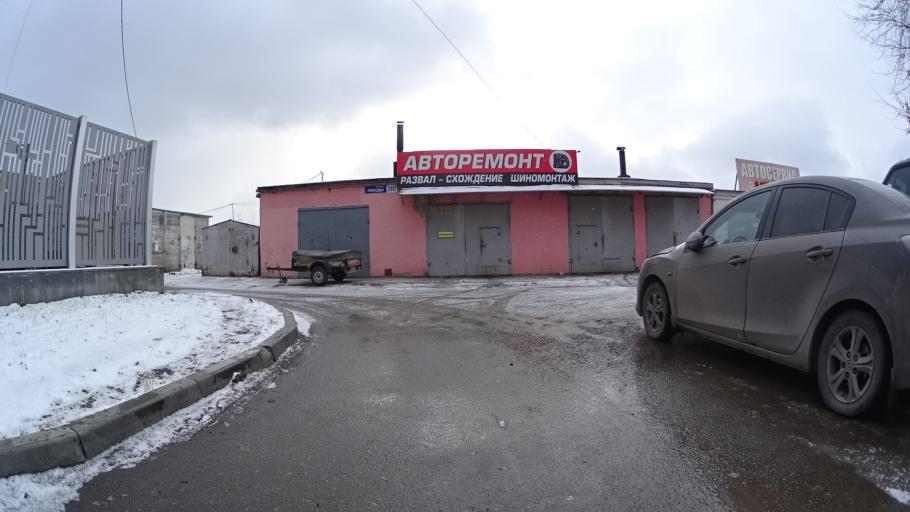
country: RU
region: Chelyabinsk
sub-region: Gorod Chelyabinsk
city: Chelyabinsk
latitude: 55.1880
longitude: 61.3189
